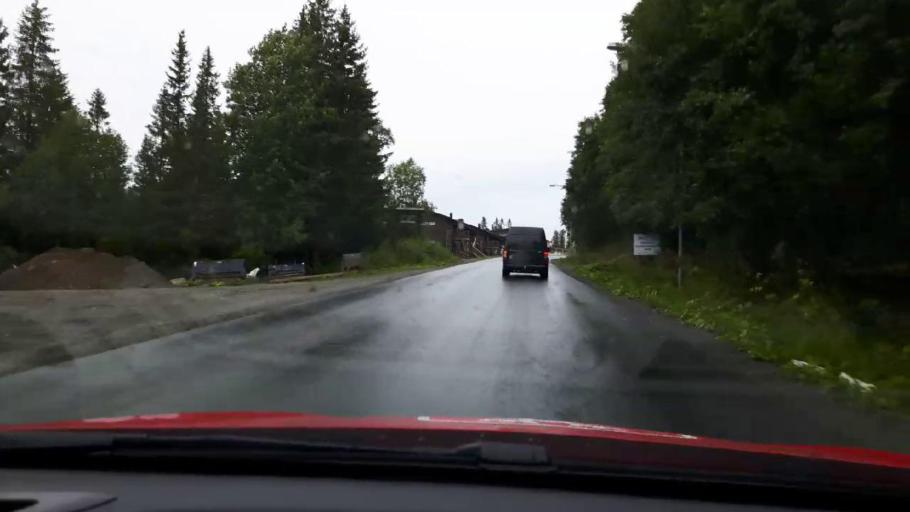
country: SE
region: Jaemtland
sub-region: Are Kommun
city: Are
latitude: 63.3838
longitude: 13.1530
